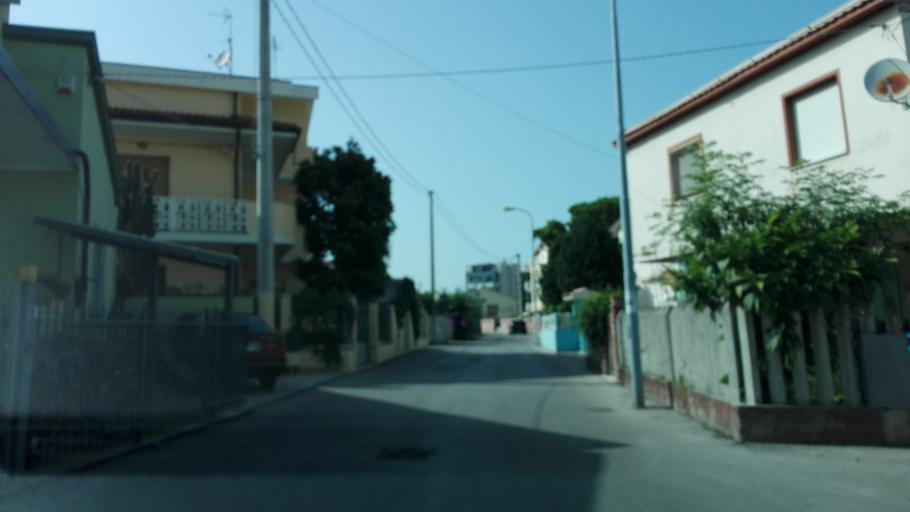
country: IT
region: Abruzzo
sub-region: Provincia di Pescara
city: Montesilvano Marina
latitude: 42.5089
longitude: 14.1394
